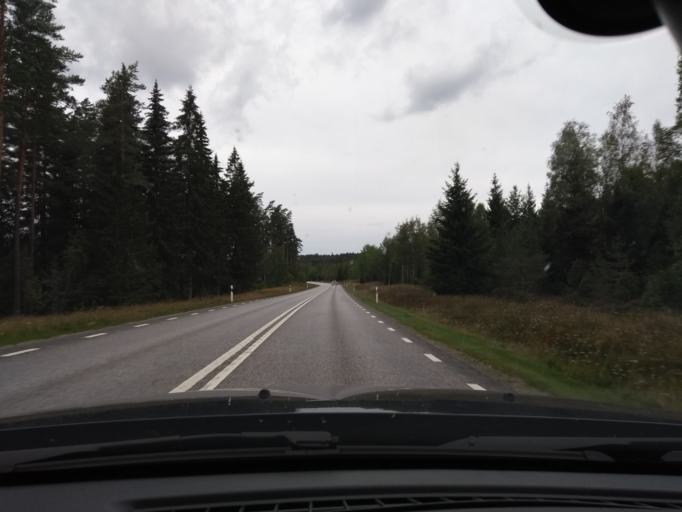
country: SE
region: OEstergoetland
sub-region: Ydre Kommun
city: OEsterbymo
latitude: 57.6425
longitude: 15.2136
